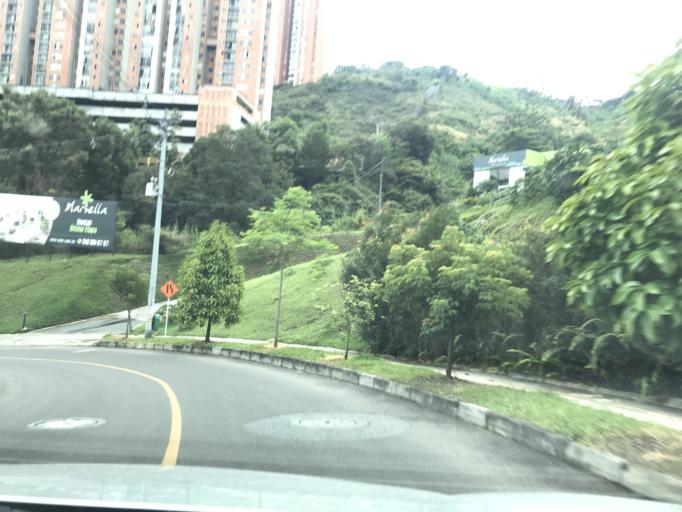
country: CO
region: Antioquia
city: Medellin
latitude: 6.2696
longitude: -75.6064
